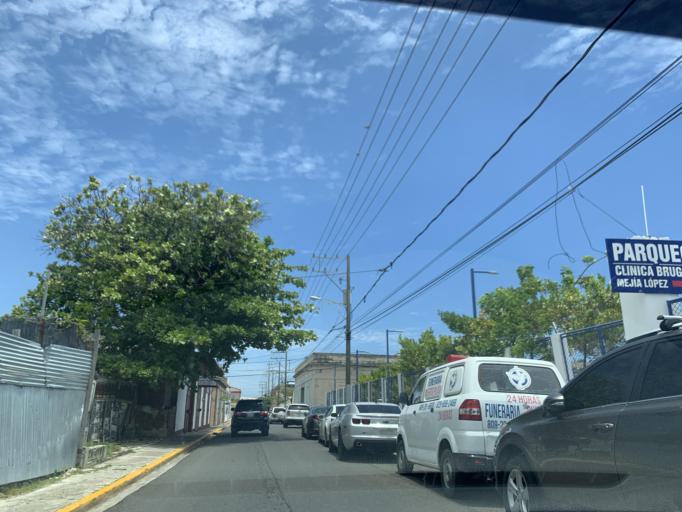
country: DO
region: Puerto Plata
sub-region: Puerto Plata
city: Puerto Plata
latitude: 19.7993
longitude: -70.6932
